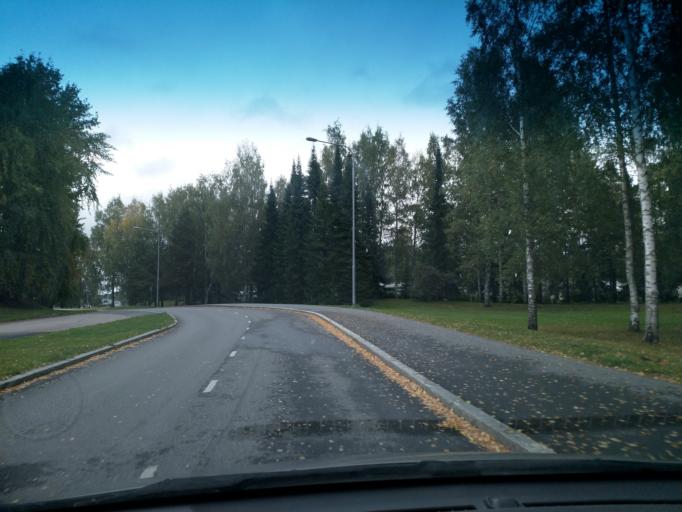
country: FI
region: Pirkanmaa
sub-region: Tampere
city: Tampere
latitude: 61.4758
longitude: 23.8424
